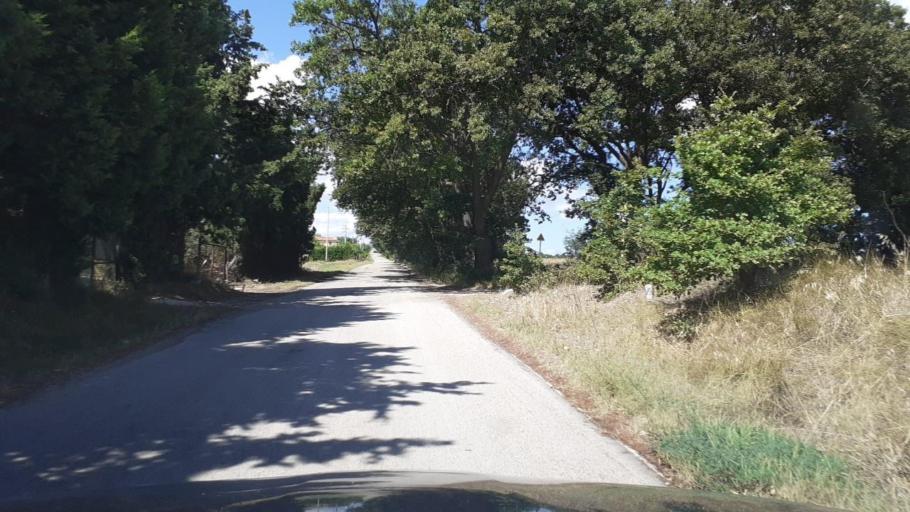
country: IT
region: Molise
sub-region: Provincia di Campobasso
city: Petacciato
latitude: 41.9988
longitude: 14.8926
